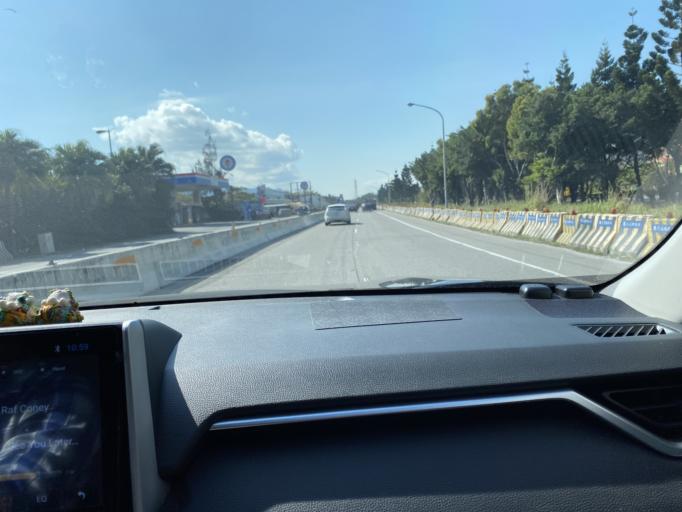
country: TW
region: Taiwan
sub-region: Hualien
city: Hualian
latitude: 23.9312
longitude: 121.5944
